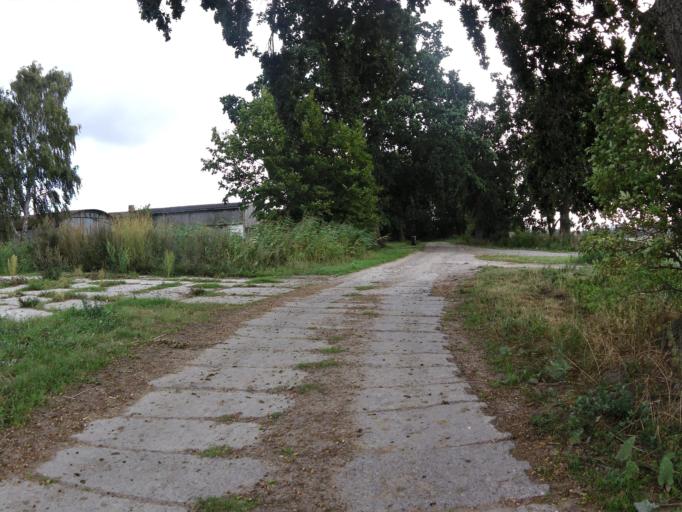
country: DE
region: Mecklenburg-Vorpommern
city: Loddin
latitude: 53.9808
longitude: 14.0648
